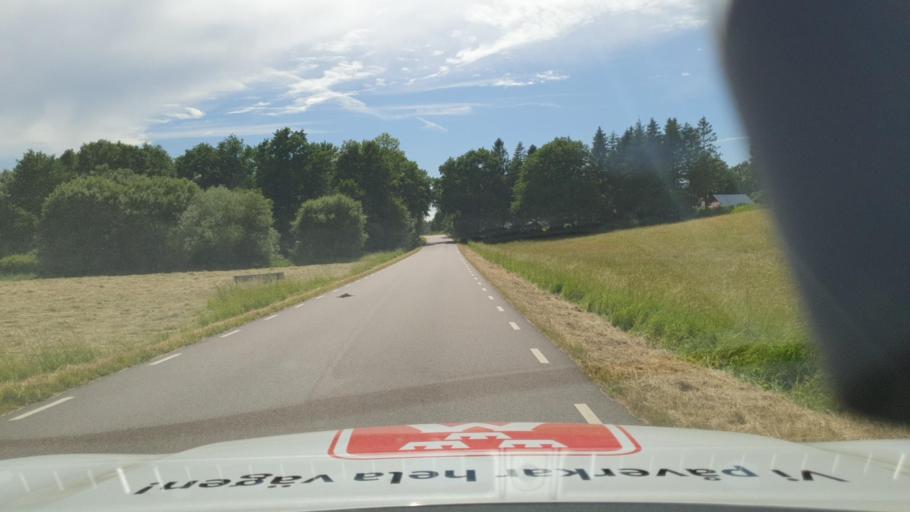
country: SE
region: Skane
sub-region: Tomelilla Kommun
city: Tomelilla
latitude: 55.6710
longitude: 13.9180
